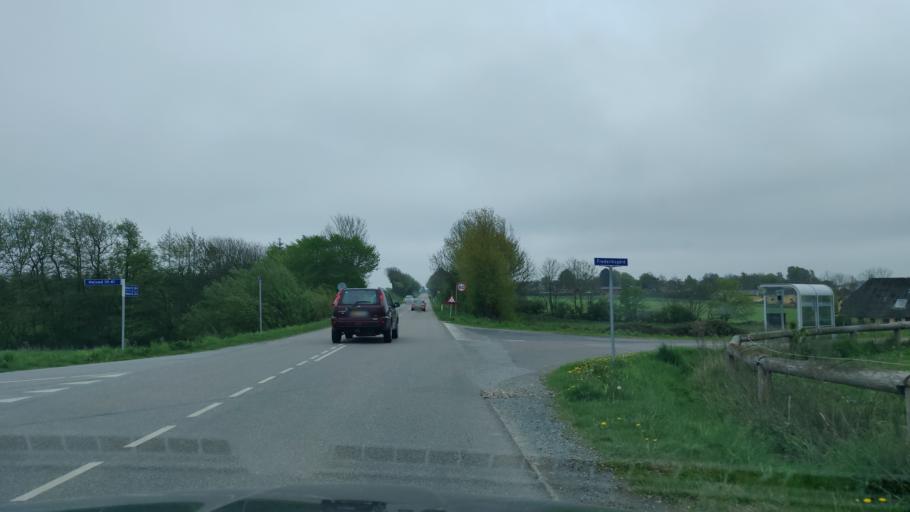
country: DK
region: South Denmark
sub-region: Sonderborg Kommune
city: Guderup
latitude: 54.9983
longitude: 9.9541
